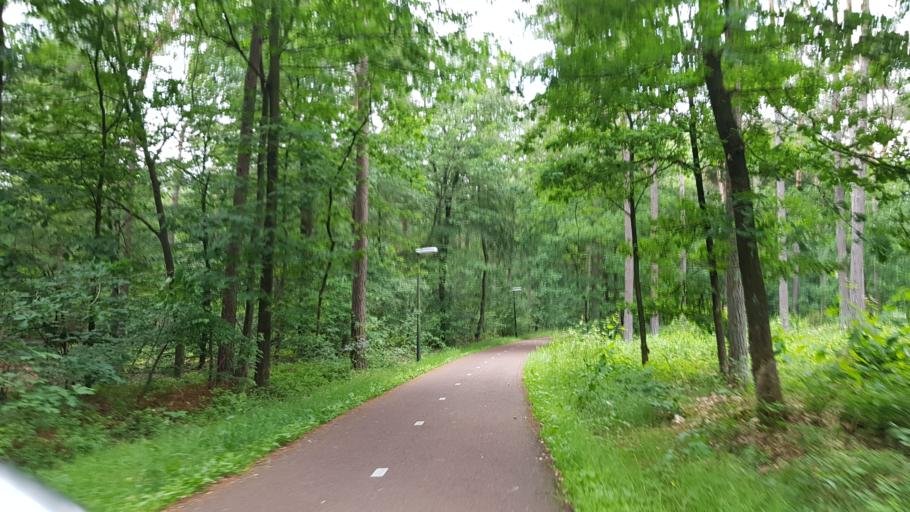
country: NL
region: Gelderland
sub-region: Gemeente Apeldoorn
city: Beekbergen
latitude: 52.1792
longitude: 5.9558
